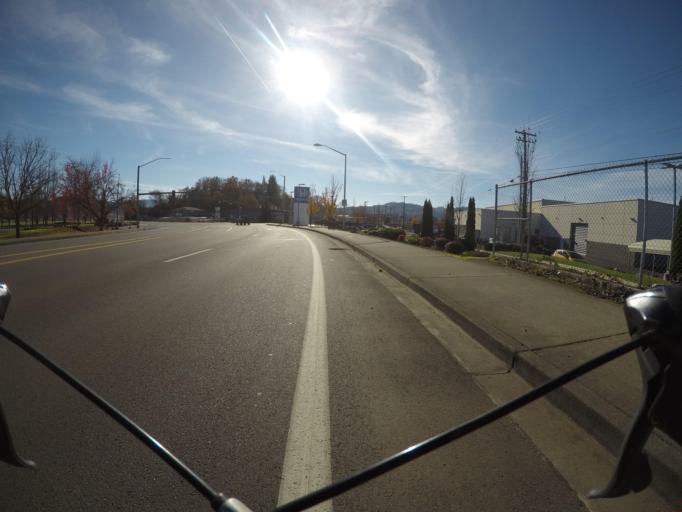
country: US
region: Oregon
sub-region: Douglas County
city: Roseburg
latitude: 43.2341
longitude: -123.3597
